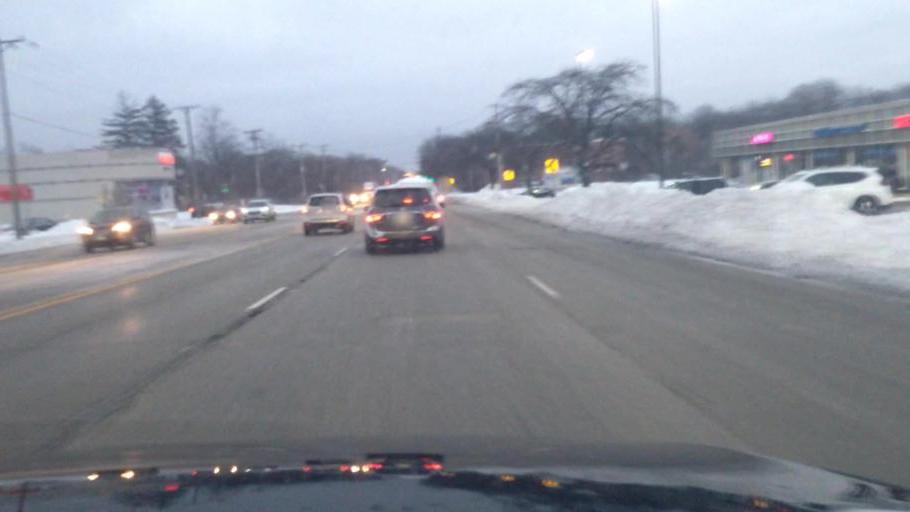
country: US
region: Illinois
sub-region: Cook County
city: Morton Grove
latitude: 42.0408
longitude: -87.7958
